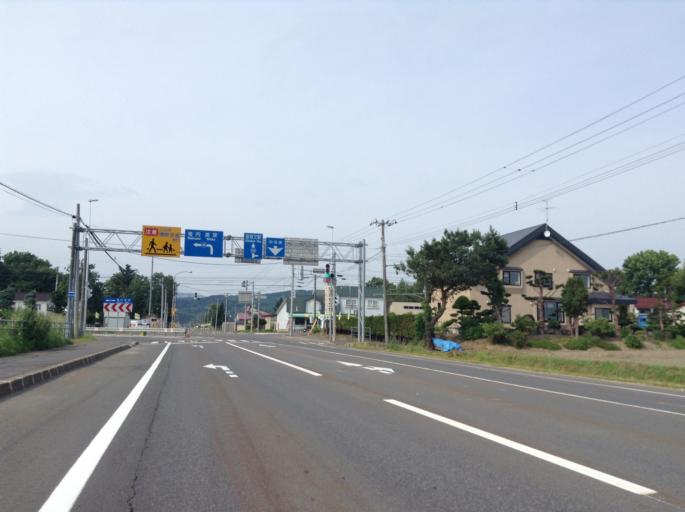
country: JP
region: Hokkaido
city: Nayoro
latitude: 44.4361
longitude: 142.4032
